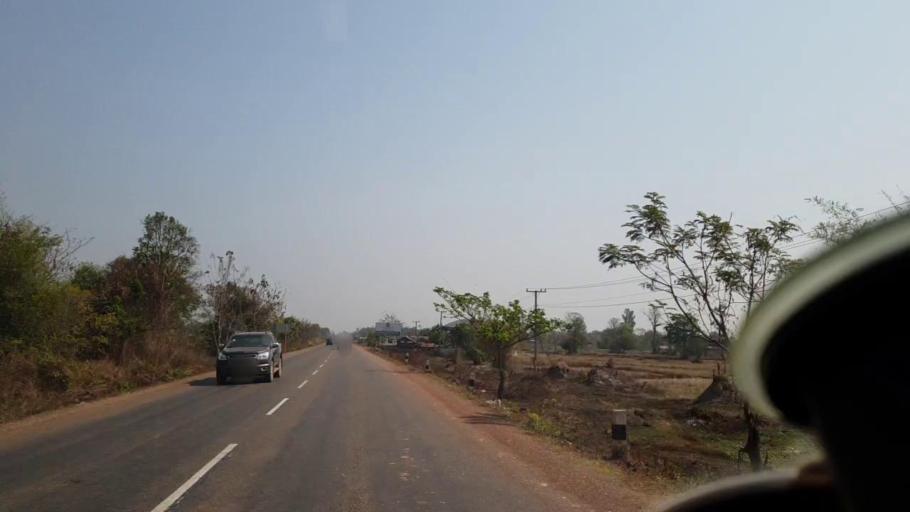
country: TH
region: Nong Khai
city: Phon Phisai
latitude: 18.0474
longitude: 102.8826
